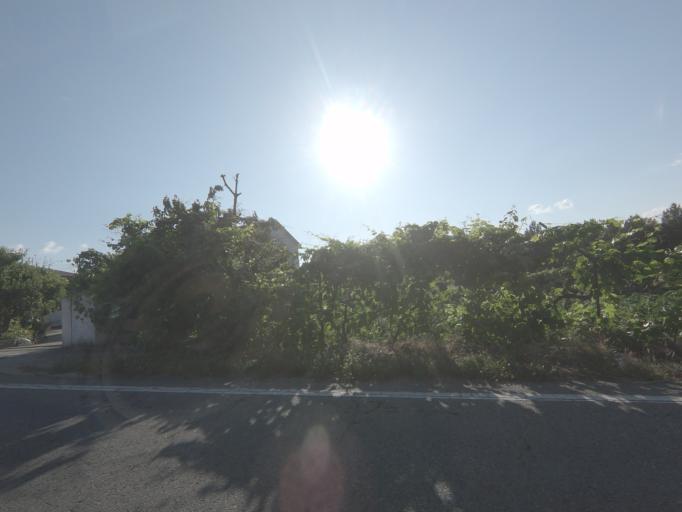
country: PT
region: Vila Real
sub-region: Chaves
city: Chaves
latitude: 41.8031
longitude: -7.4197
